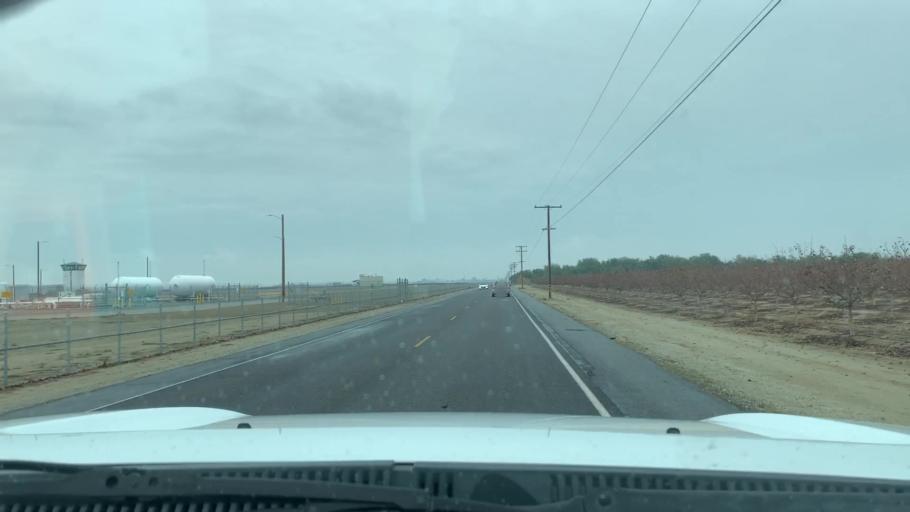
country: US
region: California
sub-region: Kern County
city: Delano
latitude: 35.7612
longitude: -119.3239
